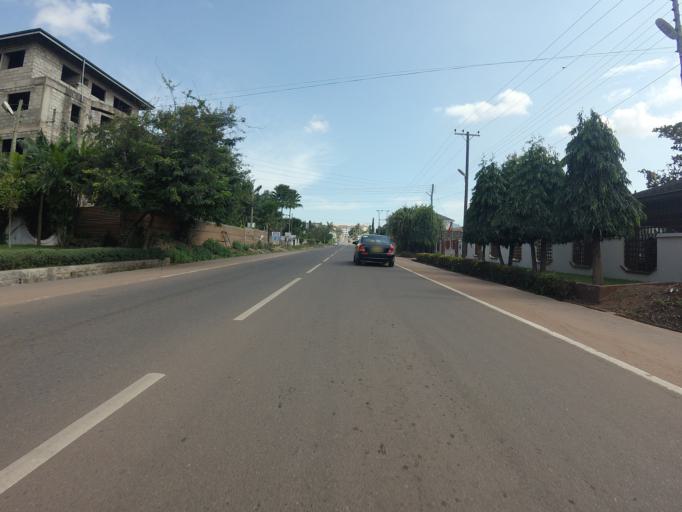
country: GH
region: Greater Accra
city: Medina Estates
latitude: 5.6719
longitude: -0.1820
